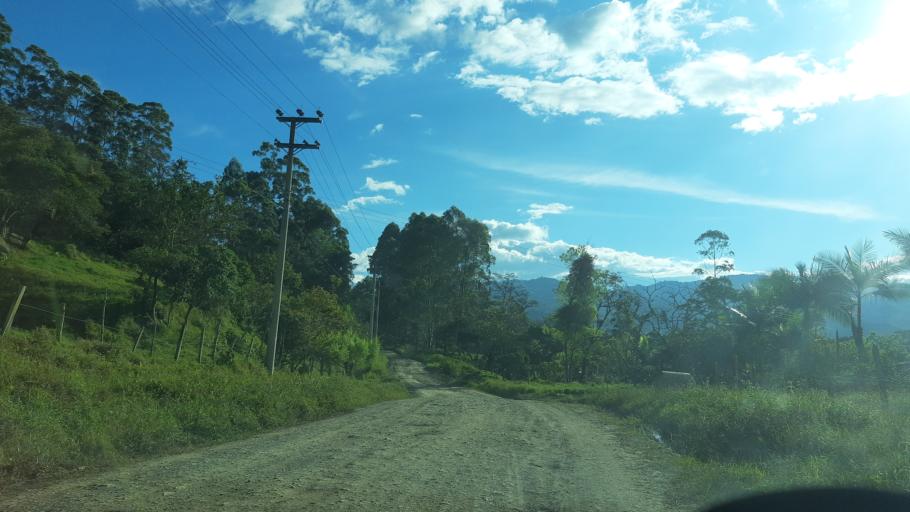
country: CO
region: Boyaca
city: Garagoa
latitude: 5.0792
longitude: -73.3723
